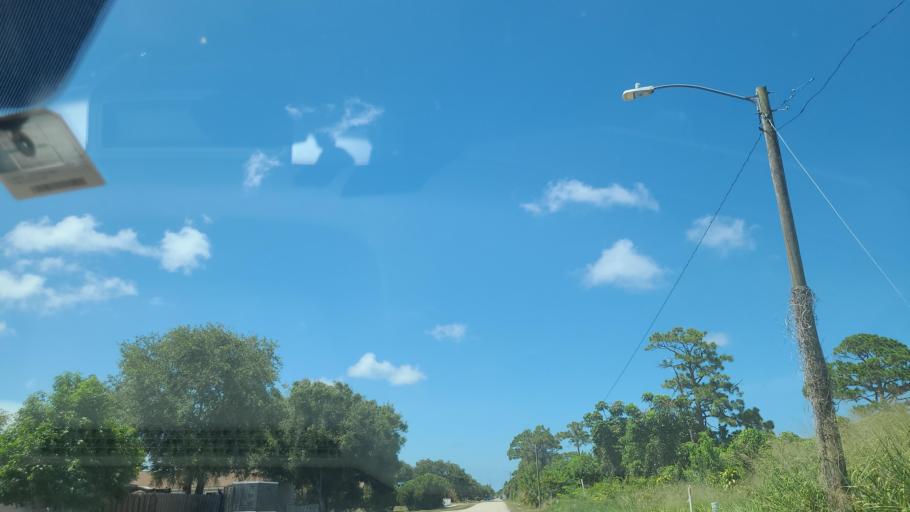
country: US
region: Florida
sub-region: Indian River County
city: Sebastian
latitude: 27.7782
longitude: -80.4619
